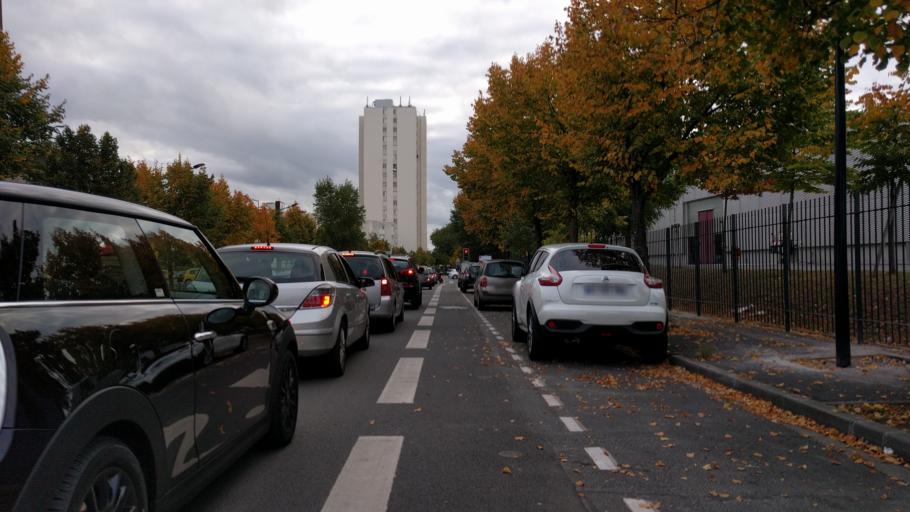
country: FR
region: Aquitaine
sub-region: Departement de la Gironde
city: Bordeaux
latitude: 44.8652
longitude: -0.5631
